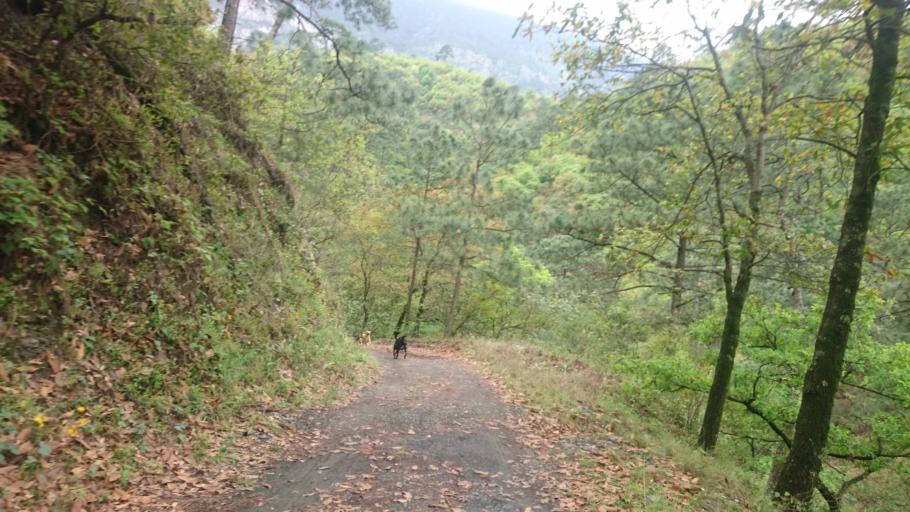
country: MX
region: Nuevo Leon
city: Garza Garcia
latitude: 25.6046
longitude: -100.3410
